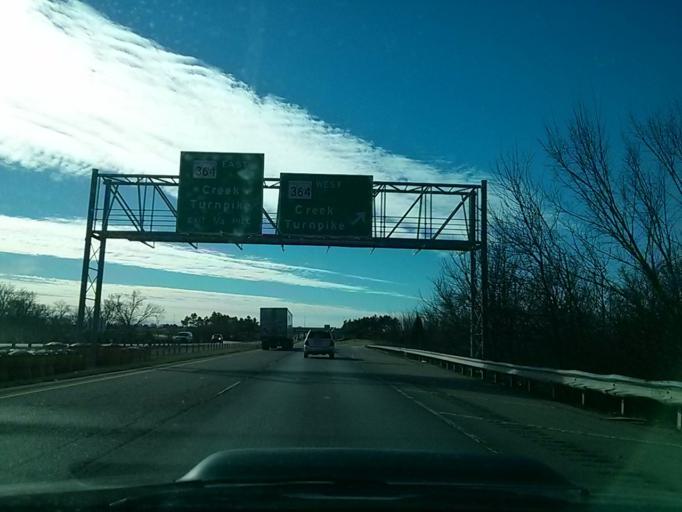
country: US
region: Oklahoma
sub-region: Tulsa County
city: Jenks
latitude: 36.0153
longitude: -96.0118
